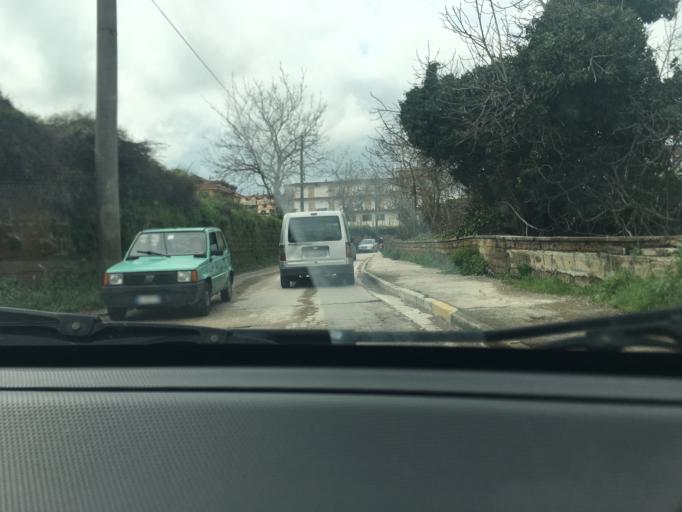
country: IT
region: Campania
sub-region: Provincia di Napoli
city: Calvizzano
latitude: 40.8955
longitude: 14.1967
